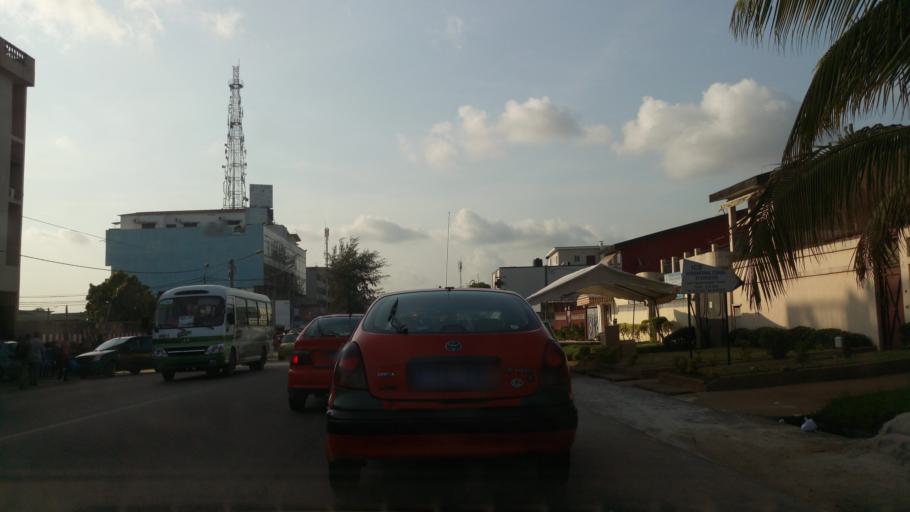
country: CI
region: Lagunes
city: Abobo
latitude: 5.4001
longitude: -3.9780
